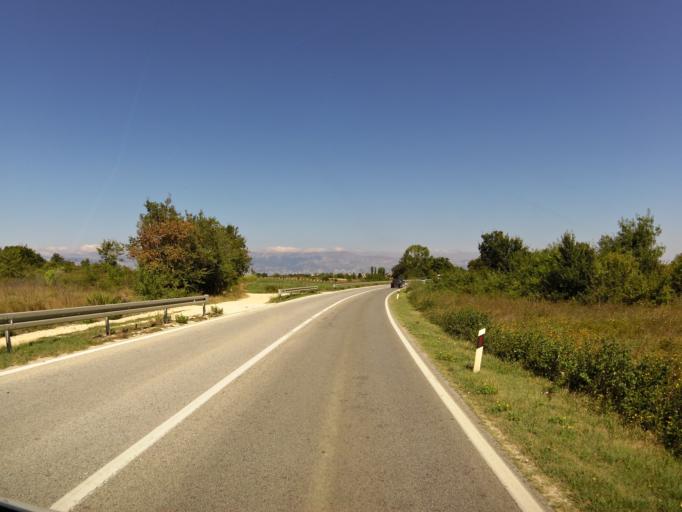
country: HR
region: Zadarska
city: Policnik
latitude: 44.1801
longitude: 15.3879
